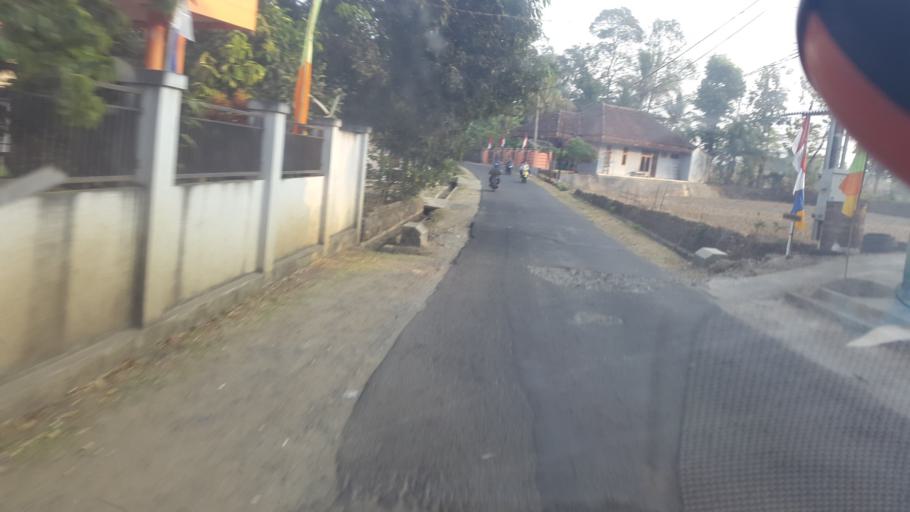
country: ID
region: West Java
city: Ciracap
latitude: -7.3342
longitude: 106.5247
